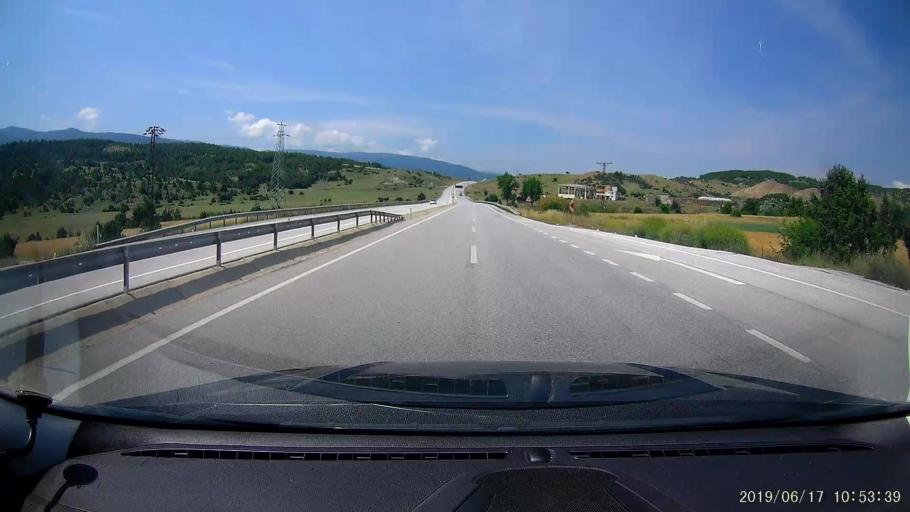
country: TR
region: Corum
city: Hacihamza
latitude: 41.0813
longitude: 34.3165
